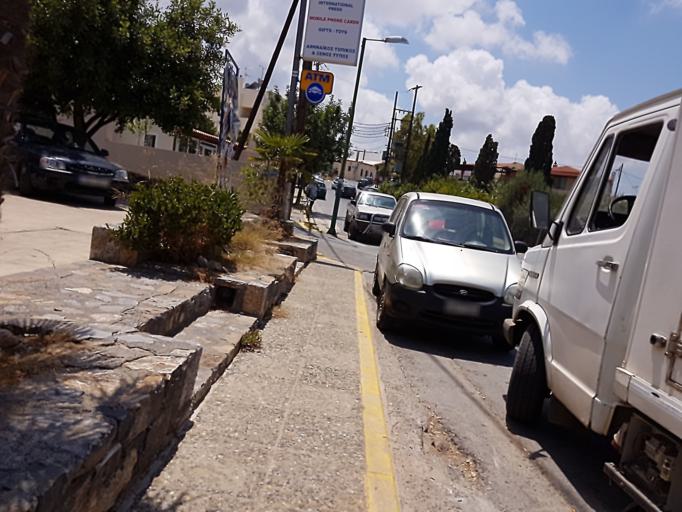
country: GR
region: Crete
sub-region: Nomos Irakleiou
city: Limin Khersonisou
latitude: 35.3087
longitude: 25.3742
